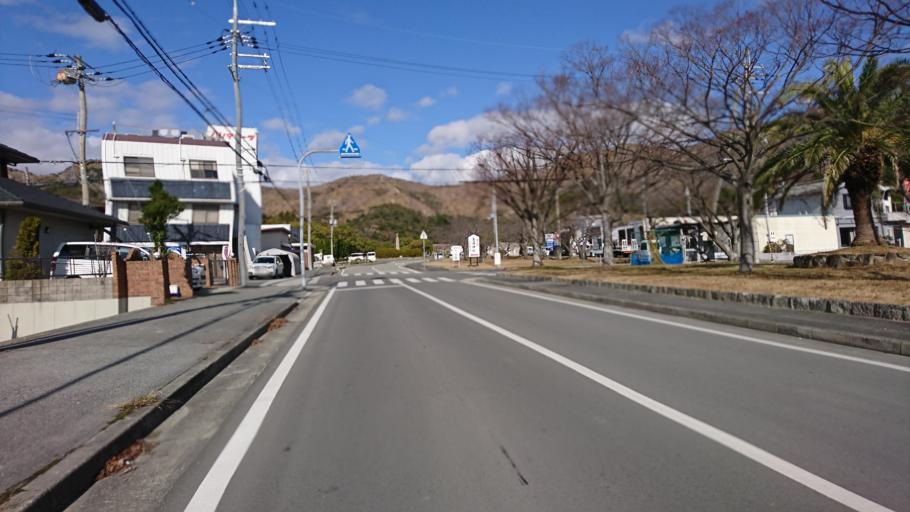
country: JP
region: Hyogo
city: Kakogawacho-honmachi
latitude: 34.8038
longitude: 134.7827
